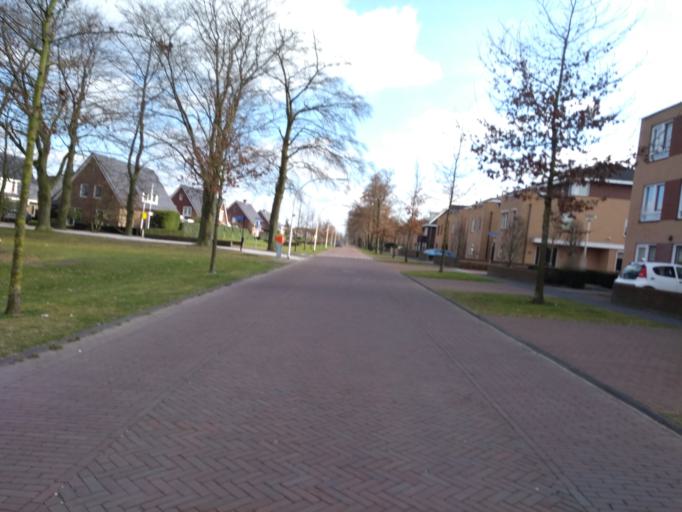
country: NL
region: Overijssel
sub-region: Gemeente Almelo
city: Almelo
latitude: 52.3476
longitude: 6.6846
